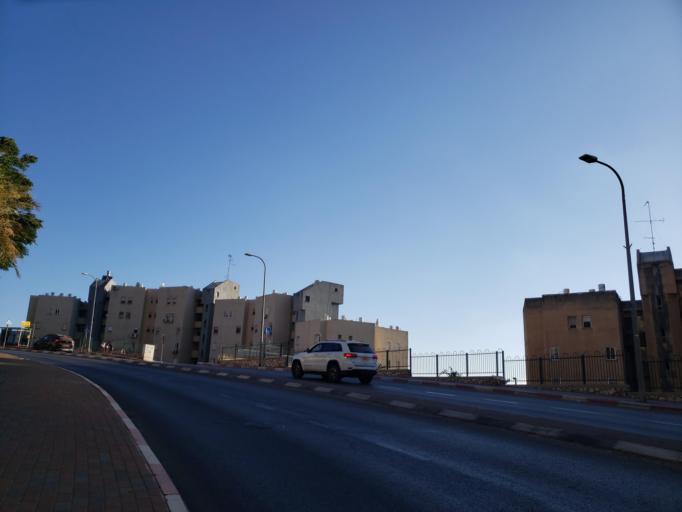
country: IL
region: Northern District
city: Safed
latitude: 32.9600
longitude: 35.4904
